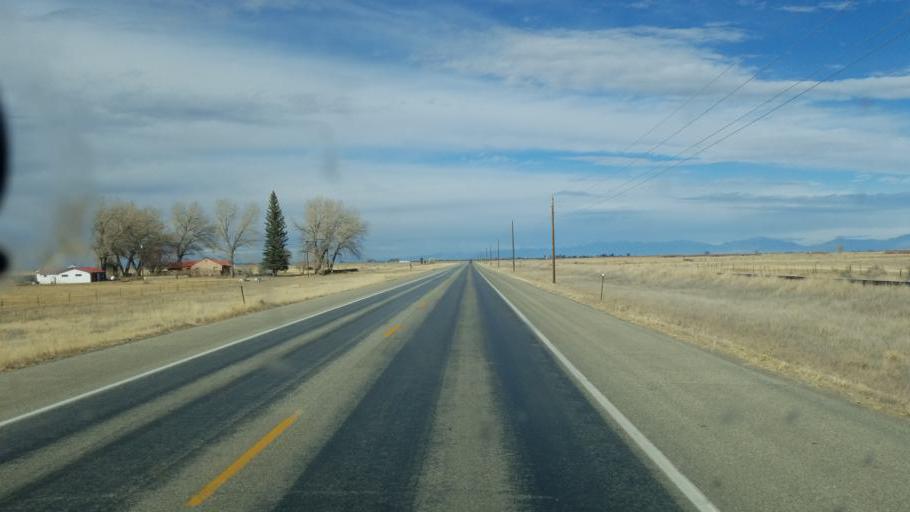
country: US
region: Colorado
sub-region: Alamosa County
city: Alamosa
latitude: 37.3102
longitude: -105.9518
